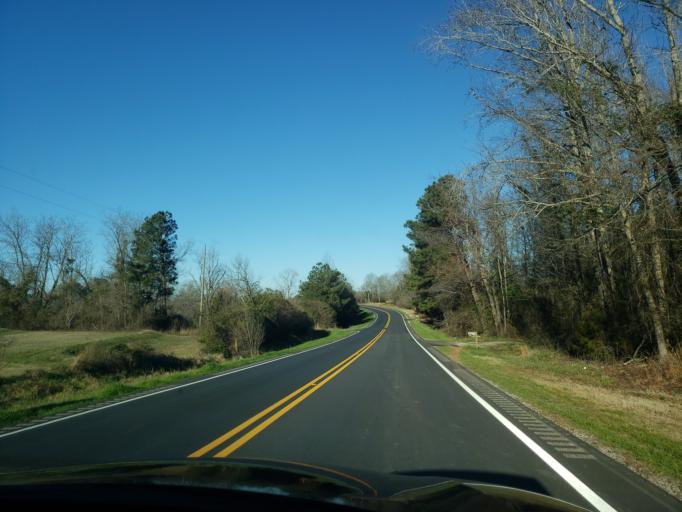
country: US
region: Alabama
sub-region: Macon County
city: Tuskegee
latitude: 32.5796
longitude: -85.7032
